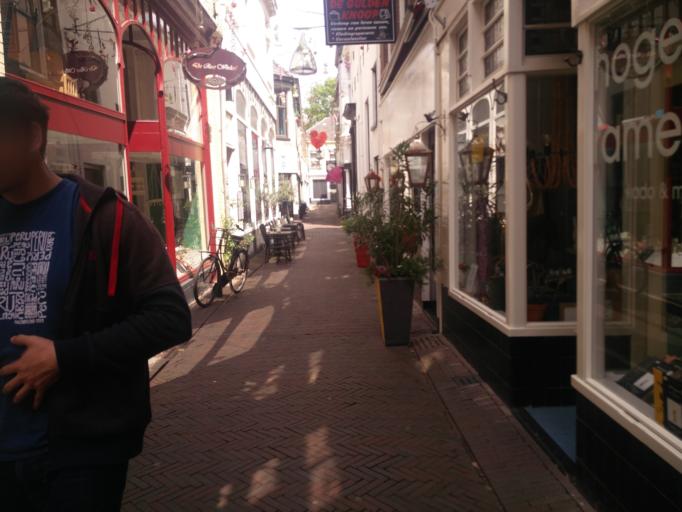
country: NL
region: Overijssel
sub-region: Gemeente Deventer
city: Deventer
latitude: 52.2523
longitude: 6.1586
